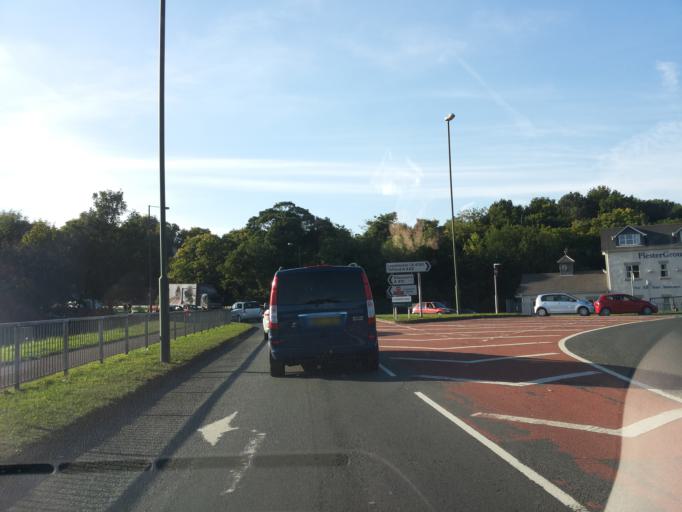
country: GB
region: England
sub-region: Worcestershire
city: Kidderminster
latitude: 52.3798
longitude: -2.2520
